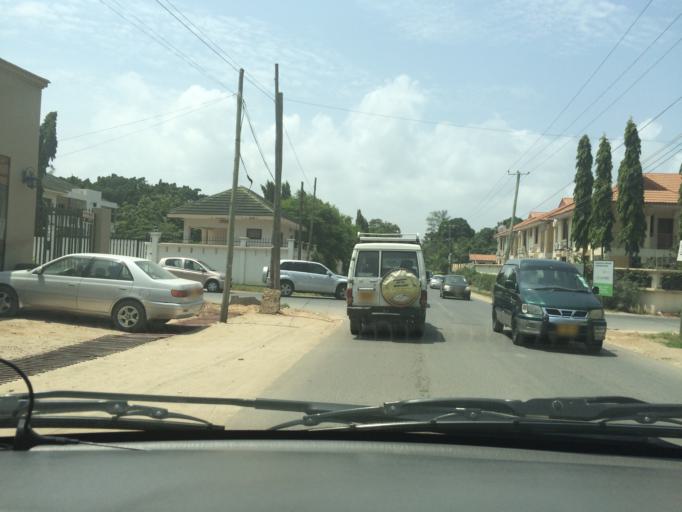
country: TZ
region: Dar es Salaam
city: Magomeni
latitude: -6.7716
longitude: 39.2630
